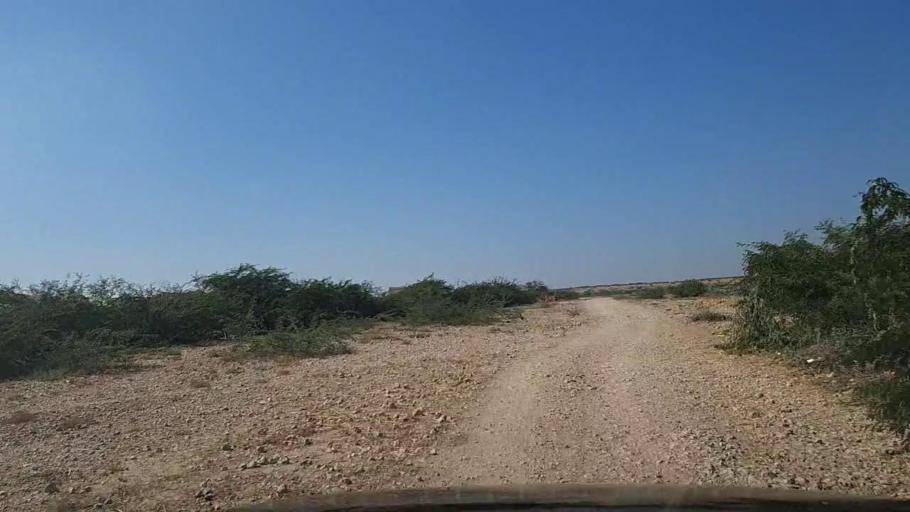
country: PK
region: Sindh
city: Thatta
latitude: 24.6290
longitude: 67.8646
